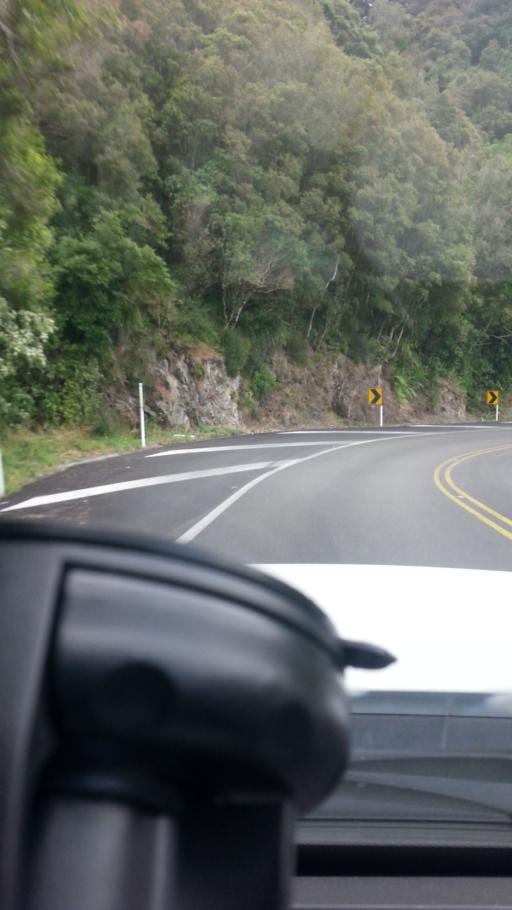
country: NZ
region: Wellington
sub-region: Upper Hutt City
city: Upper Hutt
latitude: -41.1129
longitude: 175.2175
